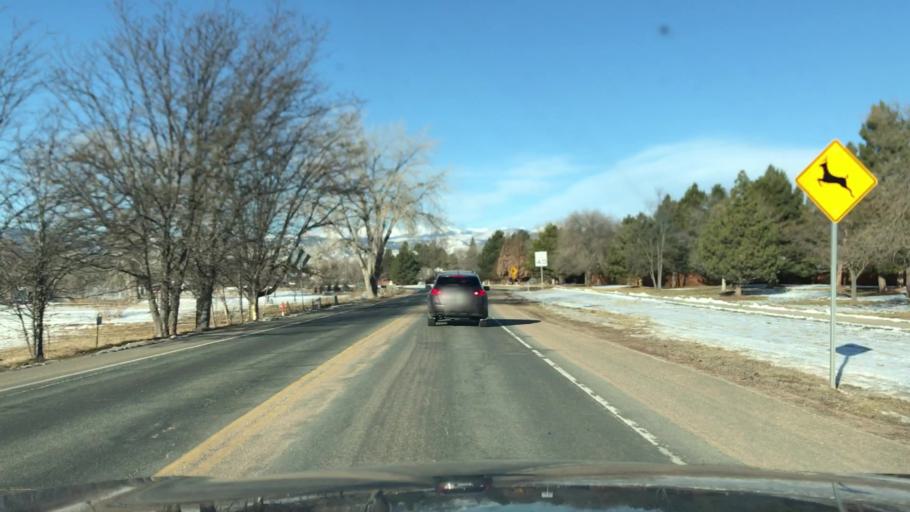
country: US
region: Colorado
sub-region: Boulder County
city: Gunbarrel
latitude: 40.0530
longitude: -105.1793
